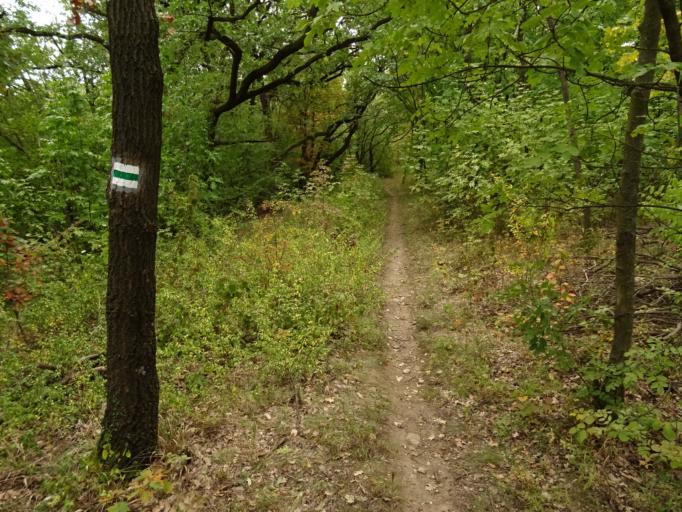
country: HU
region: Fejer
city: Kincsesbanya
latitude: 47.2204
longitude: 18.2438
